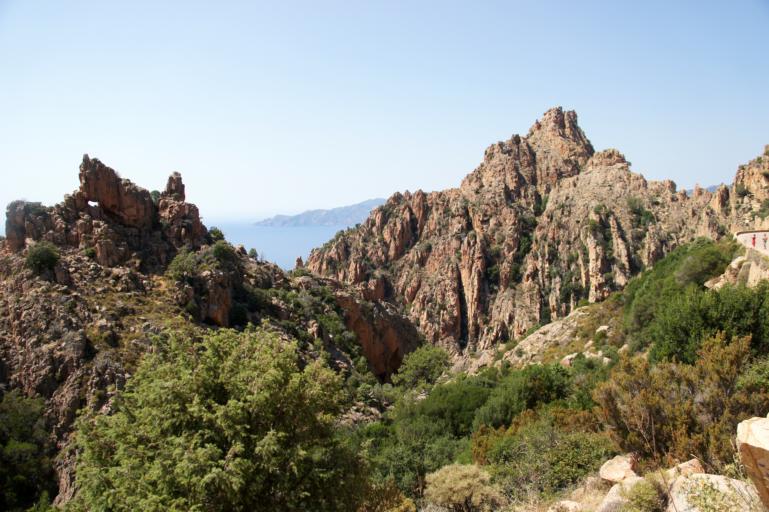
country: FR
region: Corsica
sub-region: Departement de la Corse-du-Sud
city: Cargese
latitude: 42.2429
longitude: 8.6543
